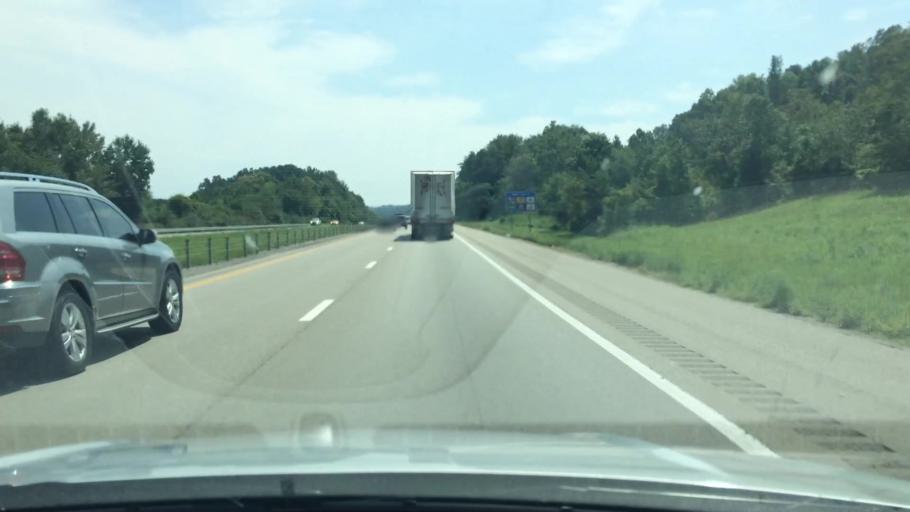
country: US
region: Kentucky
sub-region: Whitley County
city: Williamsburg
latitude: 36.7434
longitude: -84.1758
